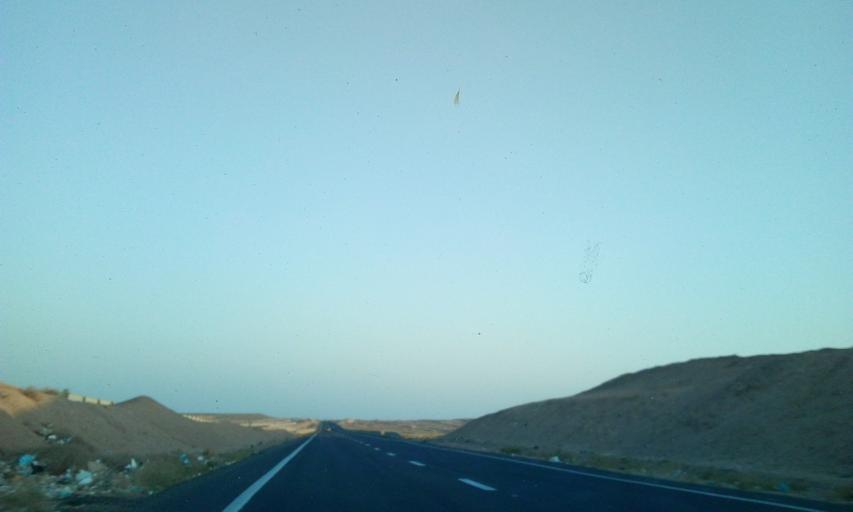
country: EG
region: Red Sea
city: El Gouna
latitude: 27.7598
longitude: 33.4943
